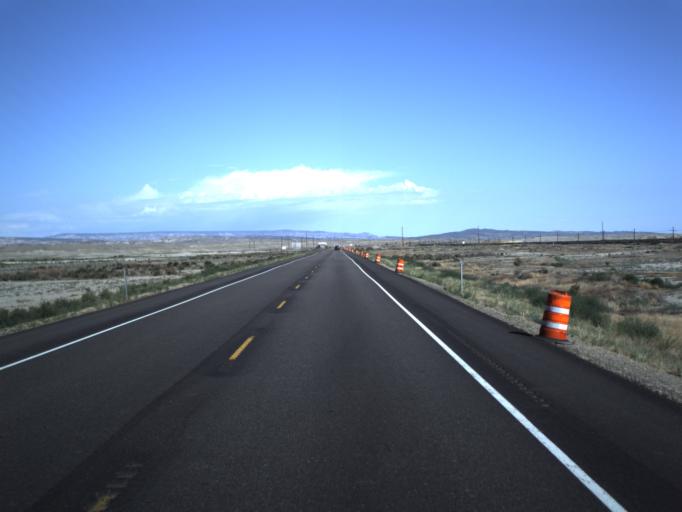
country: US
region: Utah
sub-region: Carbon County
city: East Carbon City
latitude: 39.0187
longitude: -110.2916
